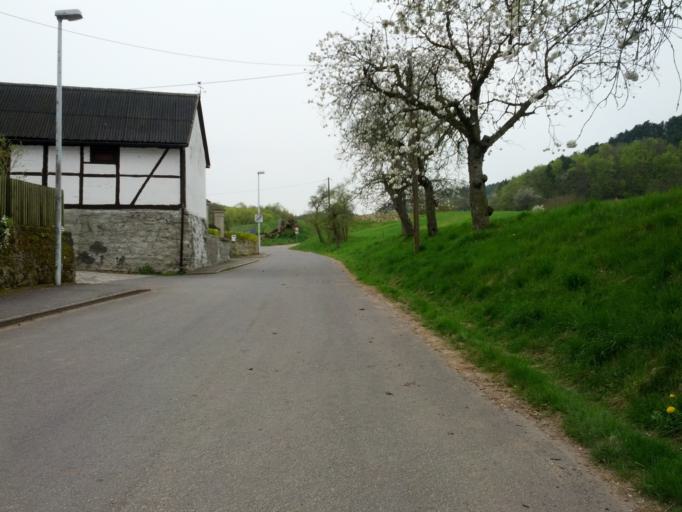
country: DE
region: Thuringia
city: Eisenach
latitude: 50.9627
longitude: 10.3634
